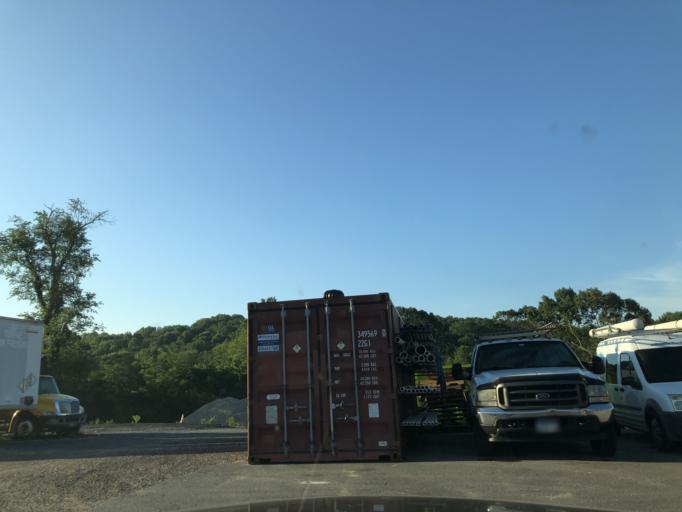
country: US
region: Maryland
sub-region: Carroll County
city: Sykesville
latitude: 39.3542
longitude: -77.0167
